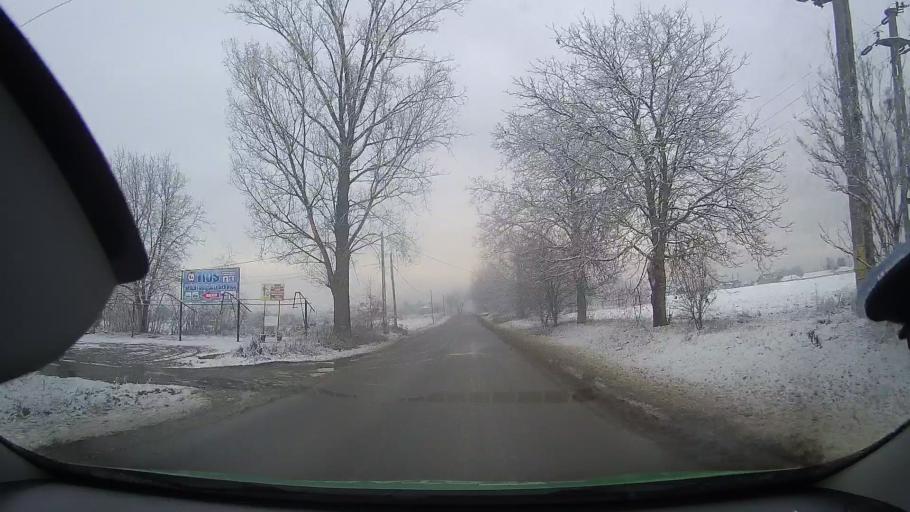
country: RO
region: Mures
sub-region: Comuna Bogata
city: Bogata
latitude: 46.4579
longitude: 24.0806
